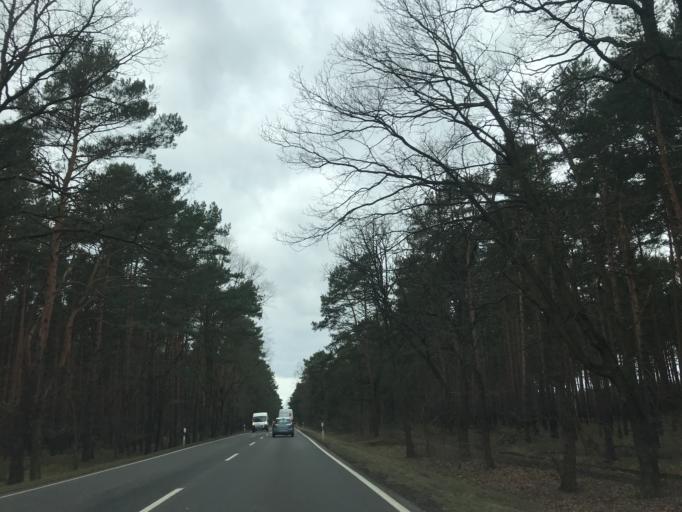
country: DE
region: Brandenburg
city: Luebben
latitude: 51.9468
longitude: 13.8533
